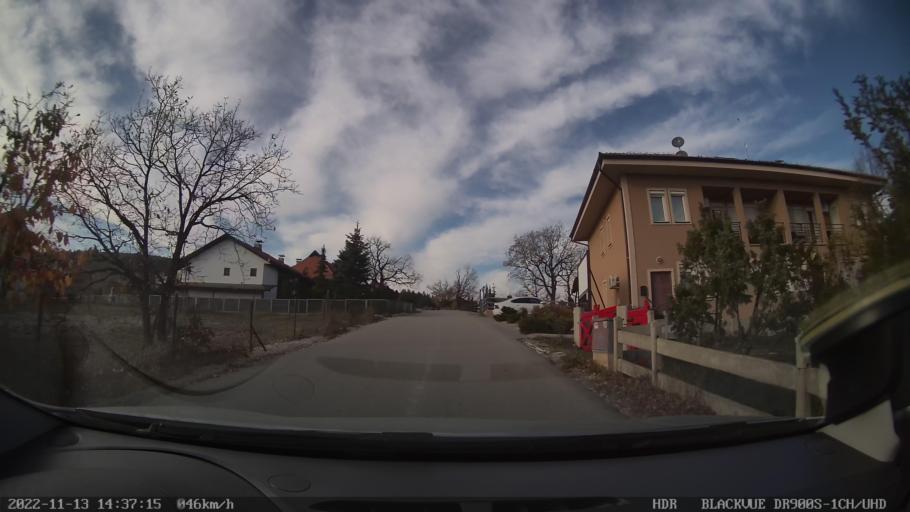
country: RS
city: Zlatibor
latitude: 43.7102
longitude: 19.7173
